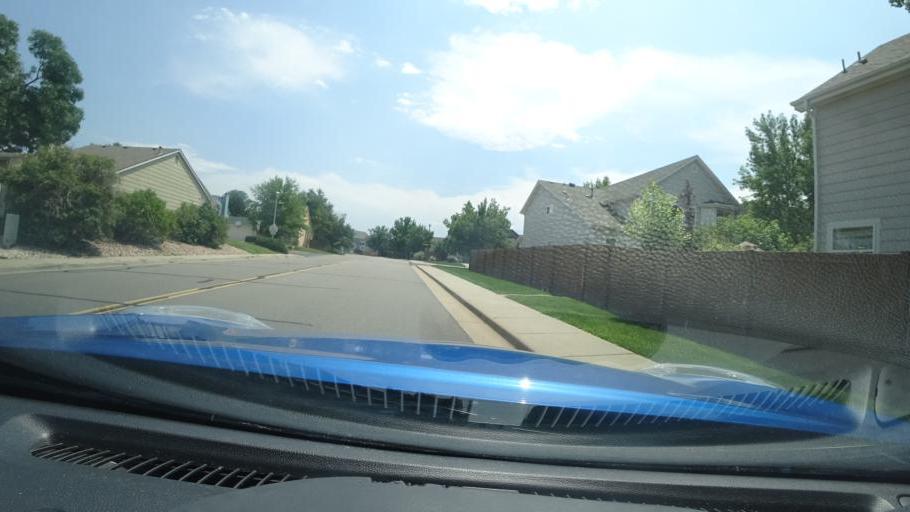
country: US
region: Colorado
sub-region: Adams County
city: Aurora
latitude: 39.6649
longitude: -104.7631
